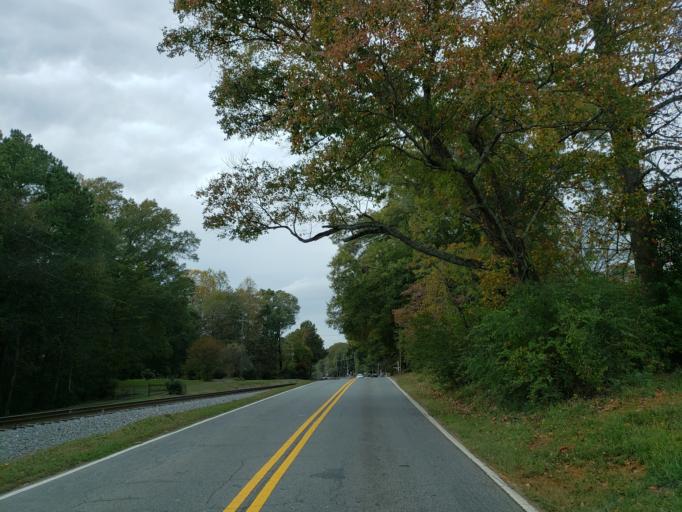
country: US
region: Georgia
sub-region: Cobb County
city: Acworth
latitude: 34.0633
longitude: -84.6578
